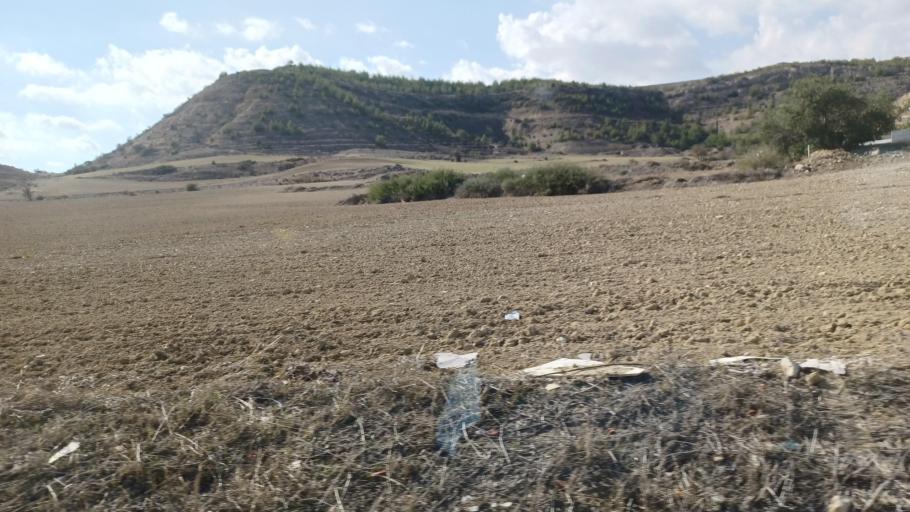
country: CY
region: Larnaka
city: Voroklini
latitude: 34.9956
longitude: 33.6552
